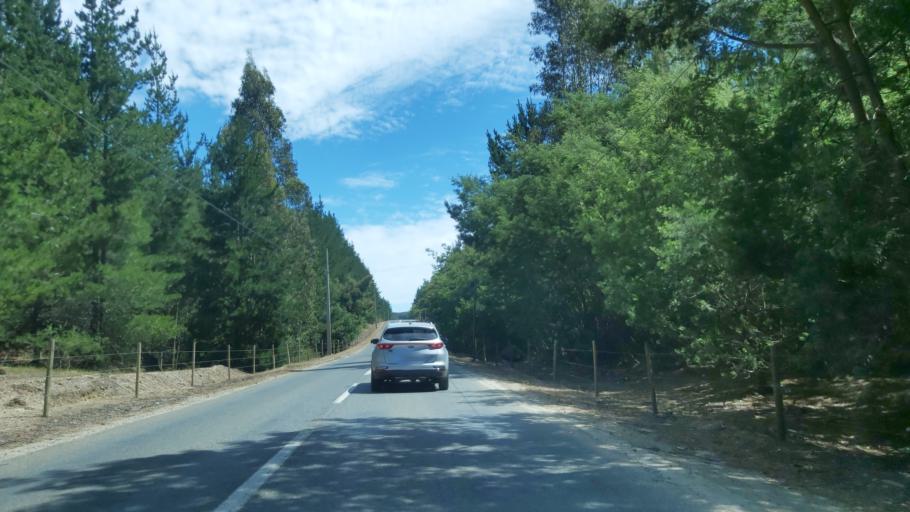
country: CL
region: Maule
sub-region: Provincia de Talca
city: Constitucion
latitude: -35.5272
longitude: -72.5394
